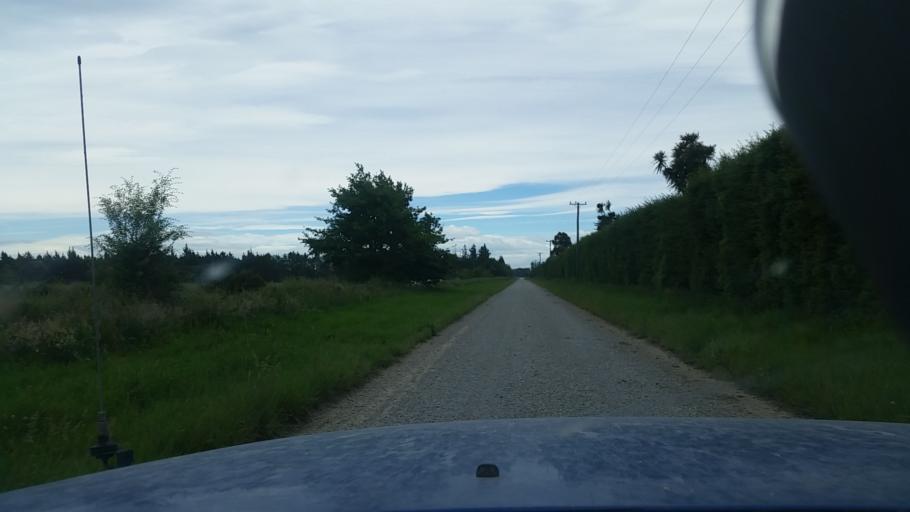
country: NZ
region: Canterbury
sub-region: Ashburton District
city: Ashburton
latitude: -43.8459
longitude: 171.6543
